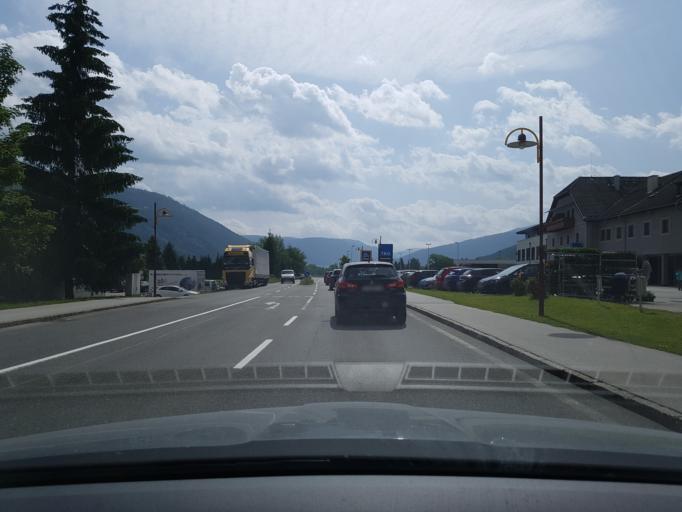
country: AT
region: Salzburg
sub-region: Politischer Bezirk Tamsweg
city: Sankt Michael im Lungau
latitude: 47.0954
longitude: 13.6379
